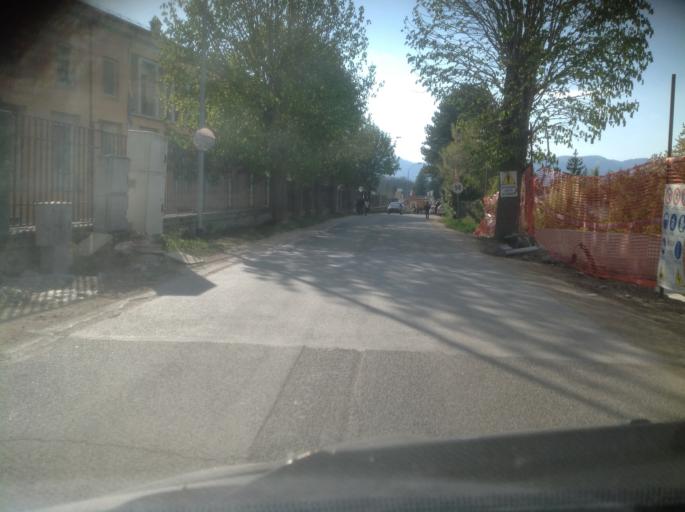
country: IT
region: Latium
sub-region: Provincia di Rieti
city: Amatrice
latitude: 42.6261
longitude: 13.2967
